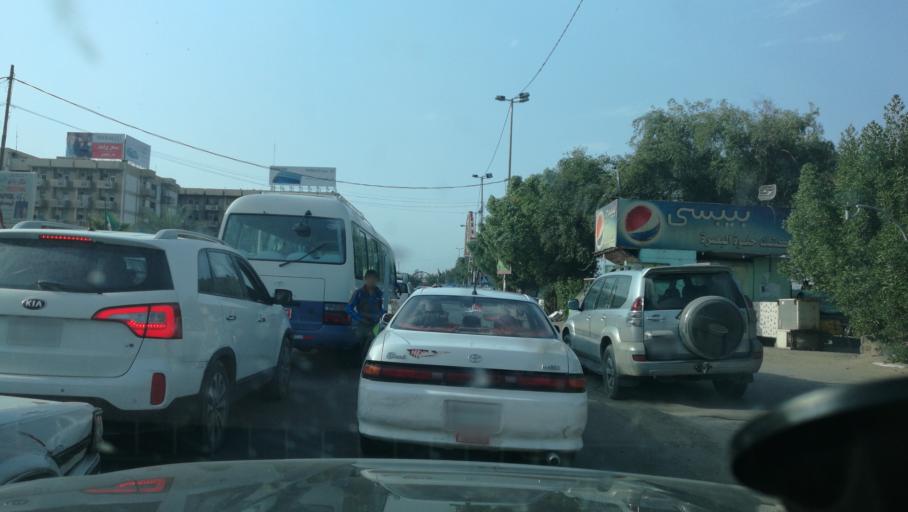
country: IQ
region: Basra Governorate
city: Al Basrah al Qadimah
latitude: 30.5207
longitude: 47.8425
